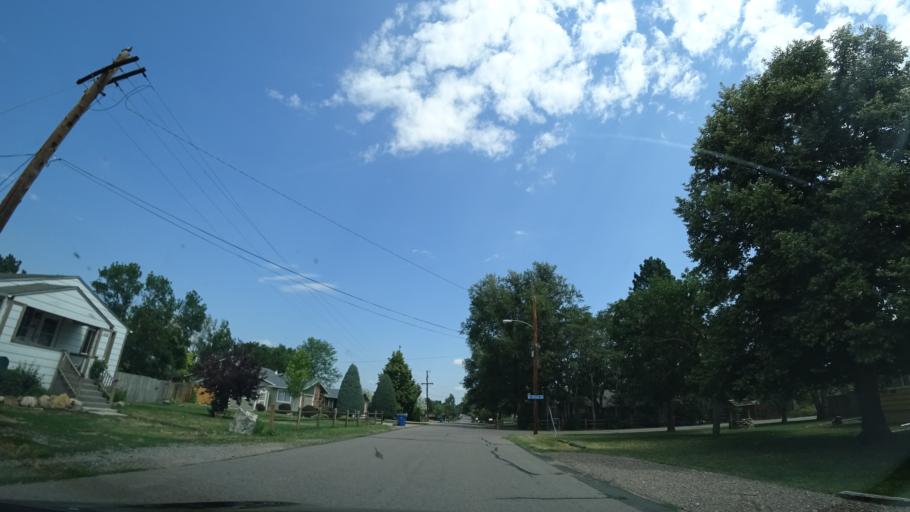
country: US
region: Colorado
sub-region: Jefferson County
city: Lakewood
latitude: 39.7145
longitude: -105.0699
